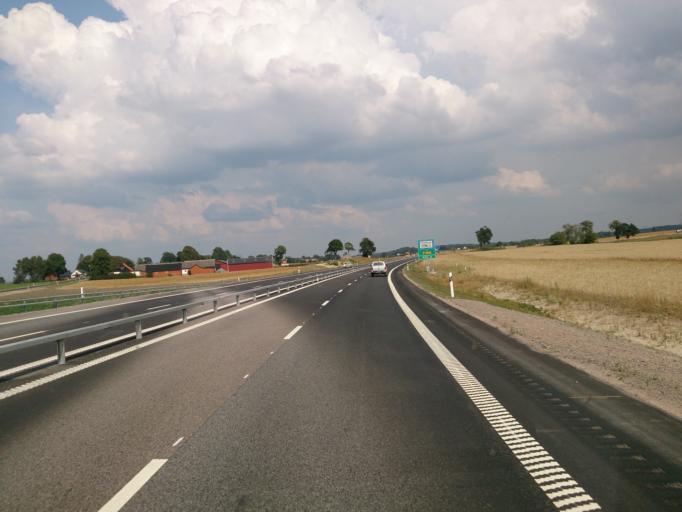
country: SE
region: Skane
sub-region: Hoors Kommun
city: Loberod
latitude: 55.8219
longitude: 13.5128
